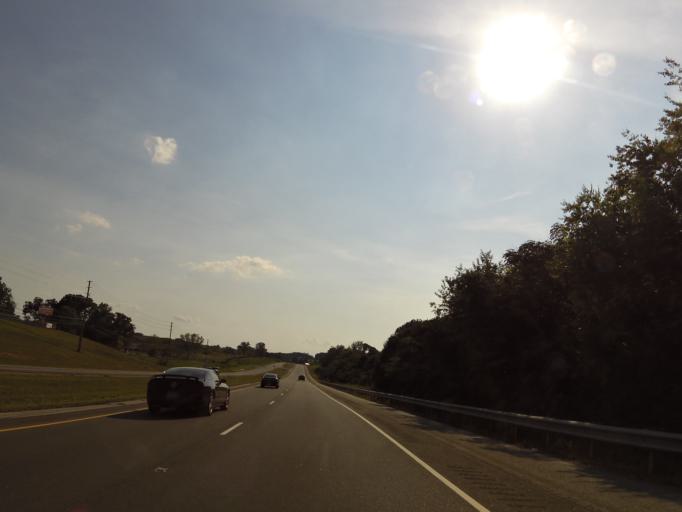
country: US
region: Tennessee
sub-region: Blount County
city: Louisville
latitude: 35.7588
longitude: -84.0691
